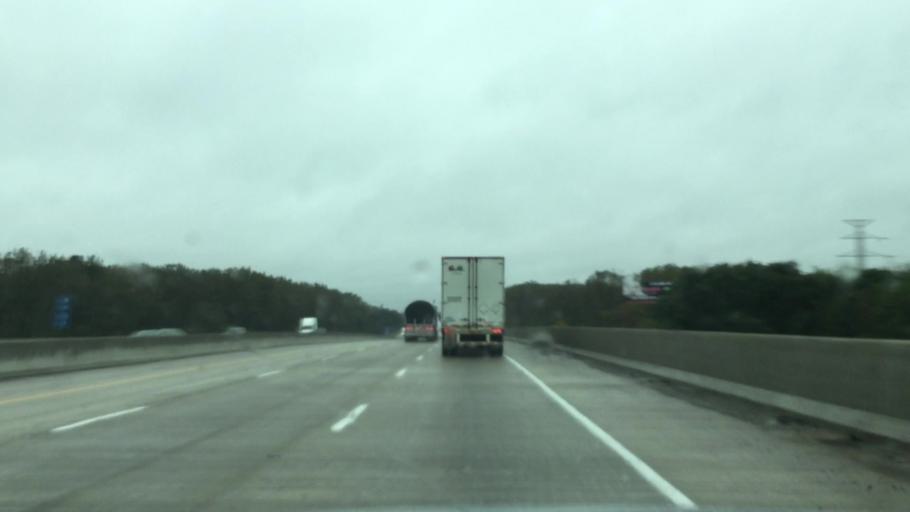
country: US
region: Indiana
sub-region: Lake County
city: Lake Station
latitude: 41.5944
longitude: -87.2169
